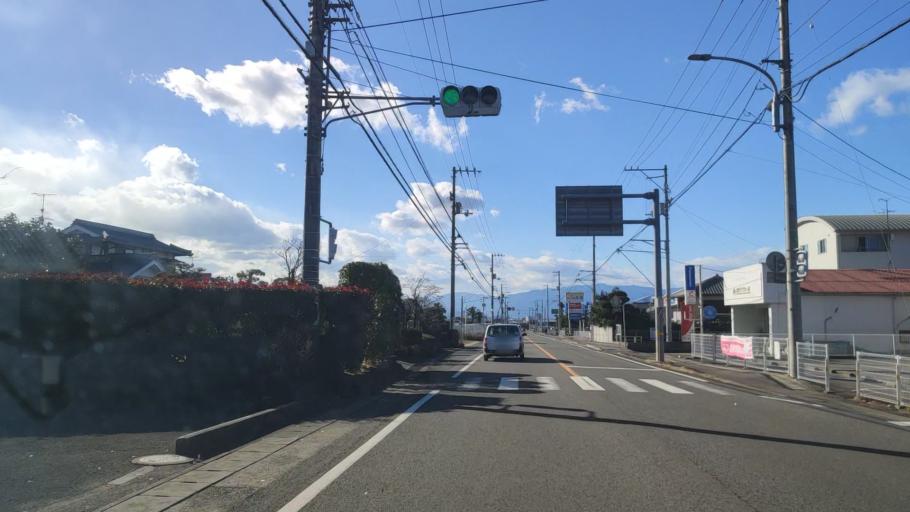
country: JP
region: Ehime
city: Saijo
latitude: 33.9182
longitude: 133.2245
